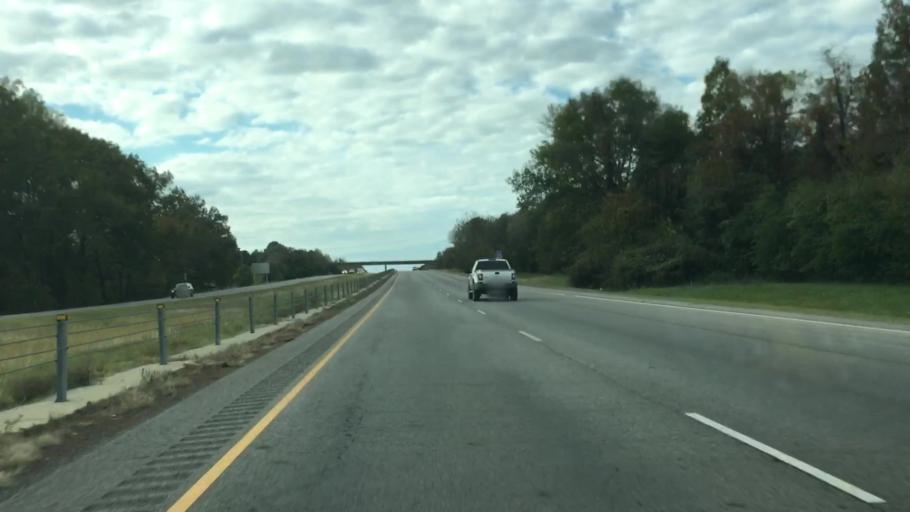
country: US
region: Arkansas
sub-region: Conway County
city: Morrilton
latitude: 35.1774
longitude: -92.7507
